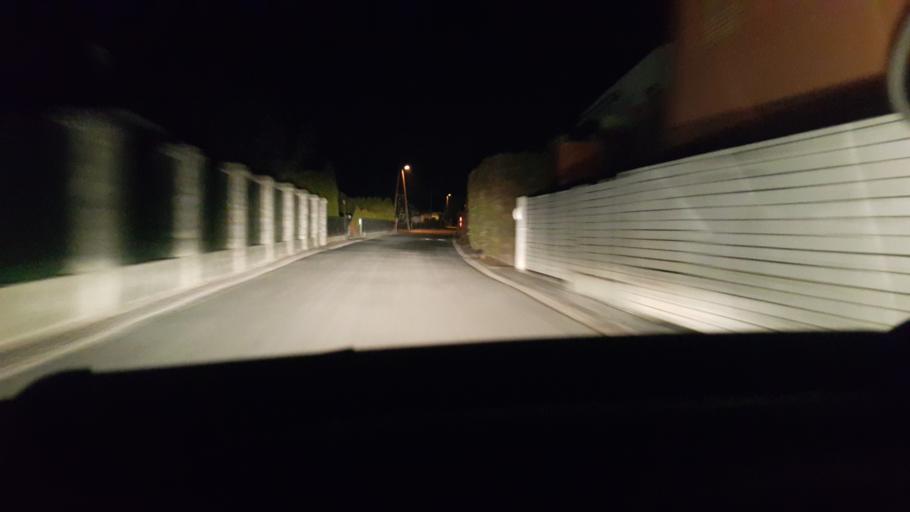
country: SI
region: Hoce-Slivnica
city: Rogoza
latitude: 46.4948
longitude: 15.6847
